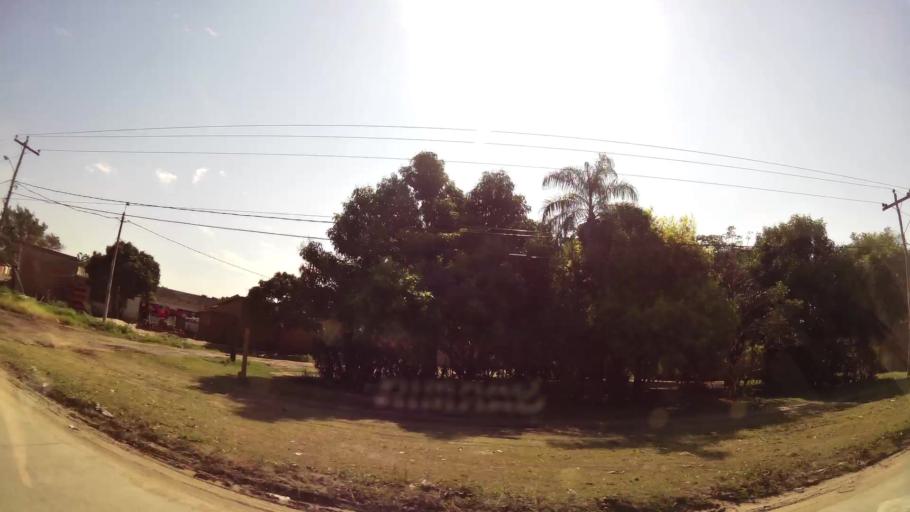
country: BO
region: Santa Cruz
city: Santa Cruz de la Sierra
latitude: -17.7621
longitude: -63.1109
